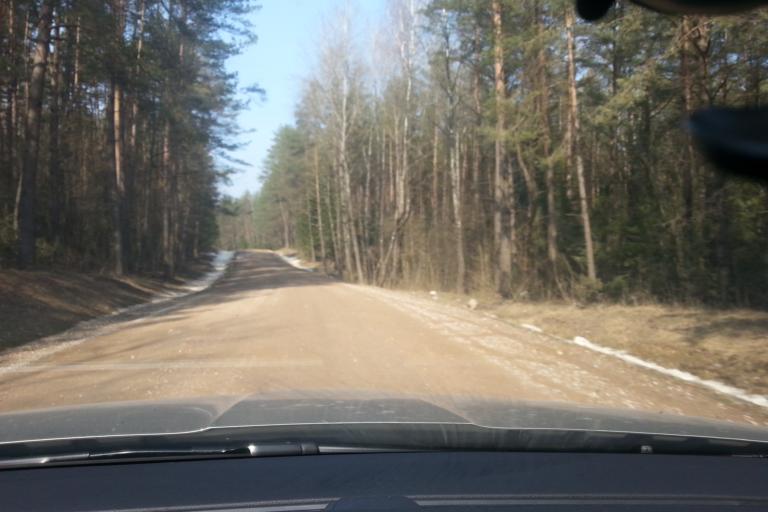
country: LT
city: Trakai
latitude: 54.5631
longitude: 24.9770
